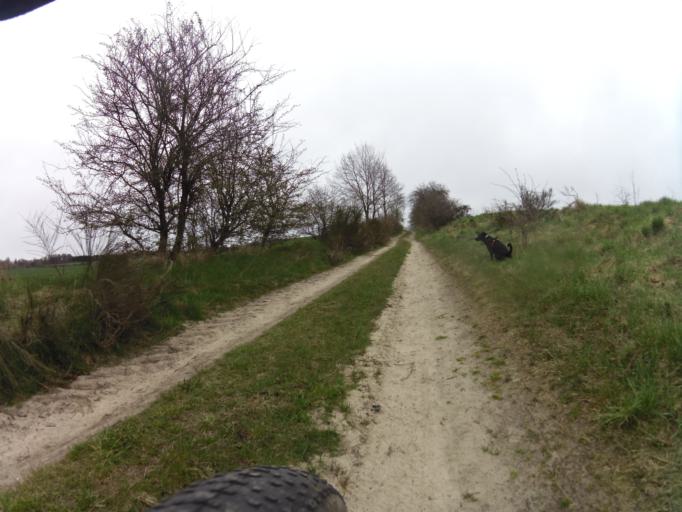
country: PL
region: West Pomeranian Voivodeship
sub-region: Powiat koszalinski
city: Polanow
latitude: 54.1602
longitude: 16.6242
